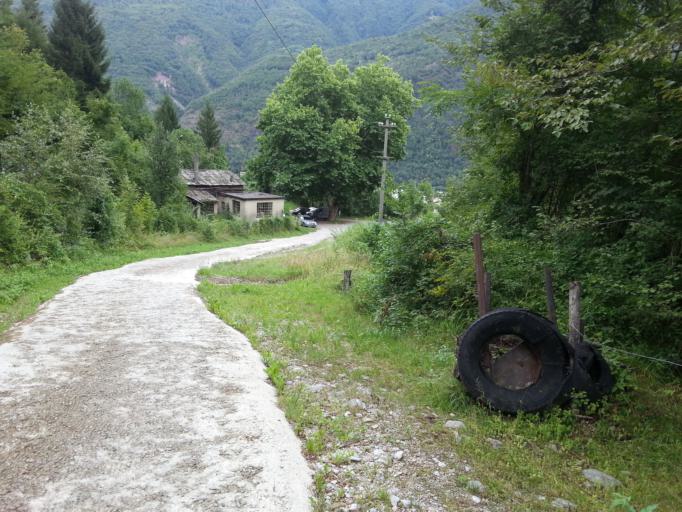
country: IT
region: Lombardy
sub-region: Provincia di Lecco
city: Cortenova
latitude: 45.9931
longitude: 9.3855
